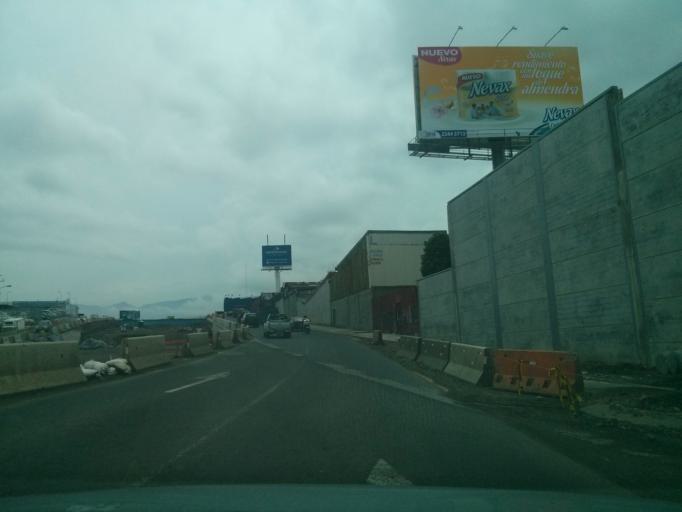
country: CR
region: San Jose
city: San Jose
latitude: 9.9115
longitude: -84.0806
